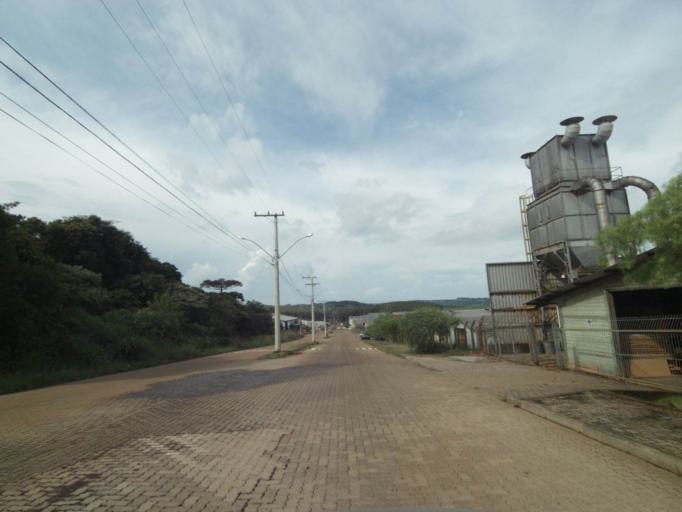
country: BR
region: Rio Grande do Sul
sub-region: Lagoa Vermelha
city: Lagoa Vermelha
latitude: -28.2285
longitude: -51.5128
